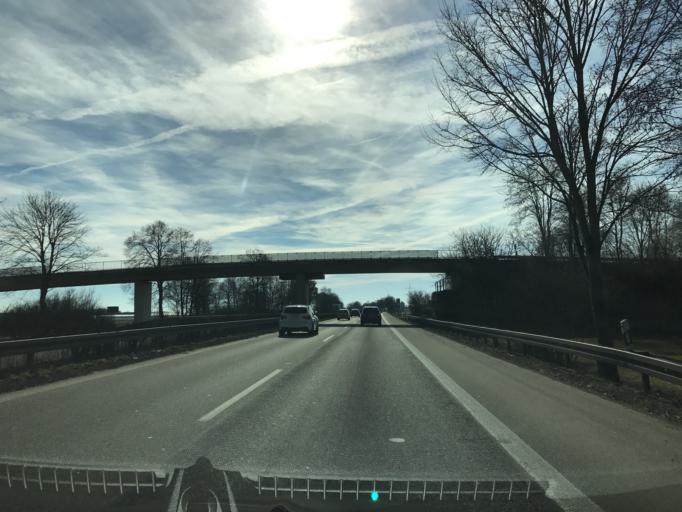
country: DE
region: Baden-Wuerttemberg
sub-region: Tuebingen Region
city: Laupheim
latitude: 48.2038
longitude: 9.8767
